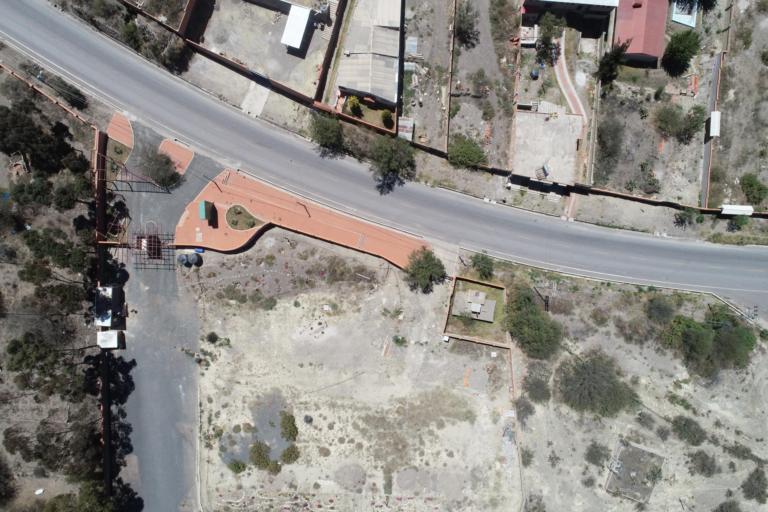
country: BO
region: La Paz
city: La Paz
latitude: -16.6203
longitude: -68.0572
